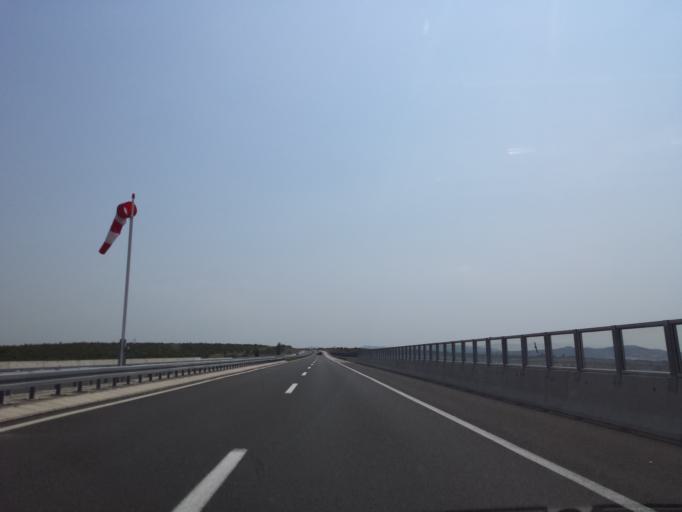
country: HR
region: Zadarska
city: Polaca
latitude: 44.0500
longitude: 15.5455
